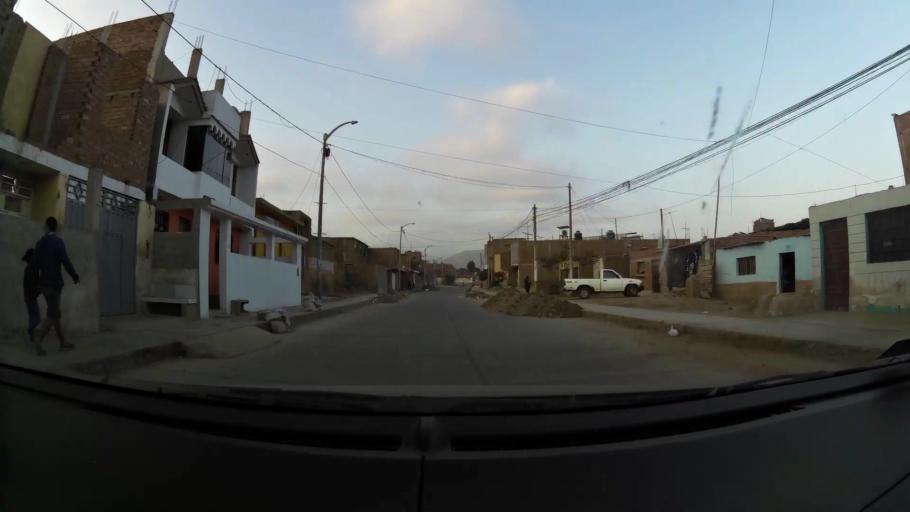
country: PE
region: La Libertad
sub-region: Provincia de Trujillo
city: El Porvenir
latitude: -8.0805
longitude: -79.0070
